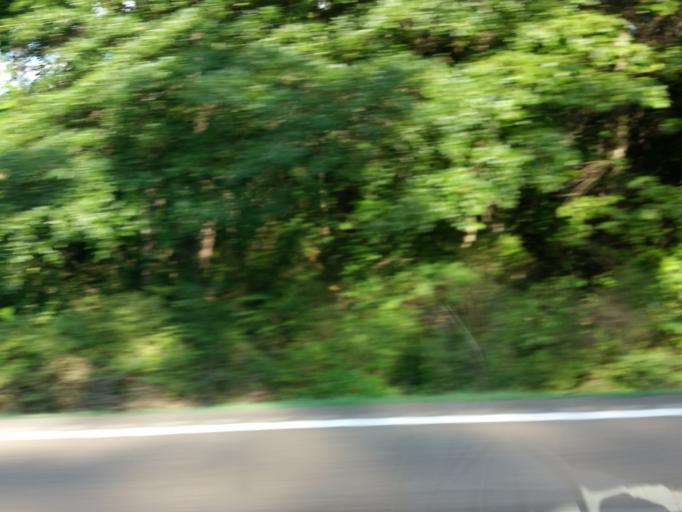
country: US
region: Mississippi
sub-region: Calhoun County
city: Calhoun City
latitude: 33.8013
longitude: -89.3551
